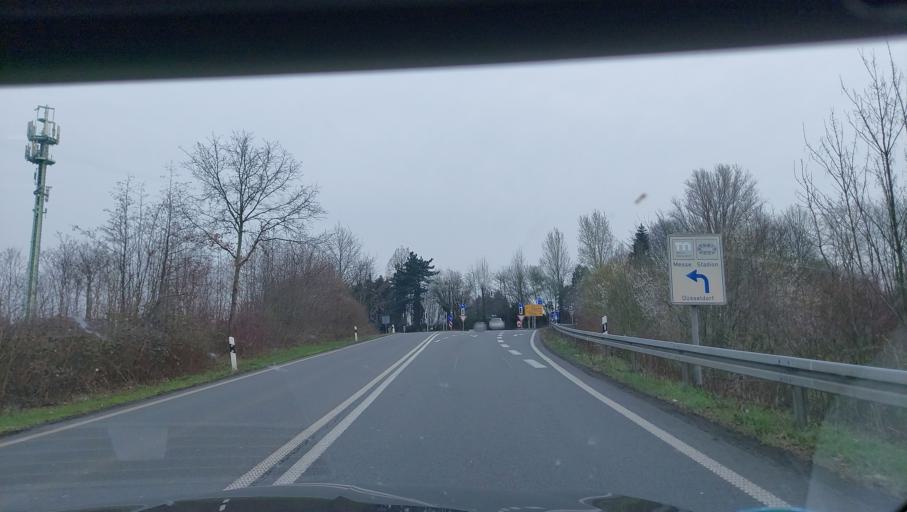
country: DE
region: North Rhine-Westphalia
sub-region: Regierungsbezirk Dusseldorf
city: Erkrath
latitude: 51.2580
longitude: 6.9160
